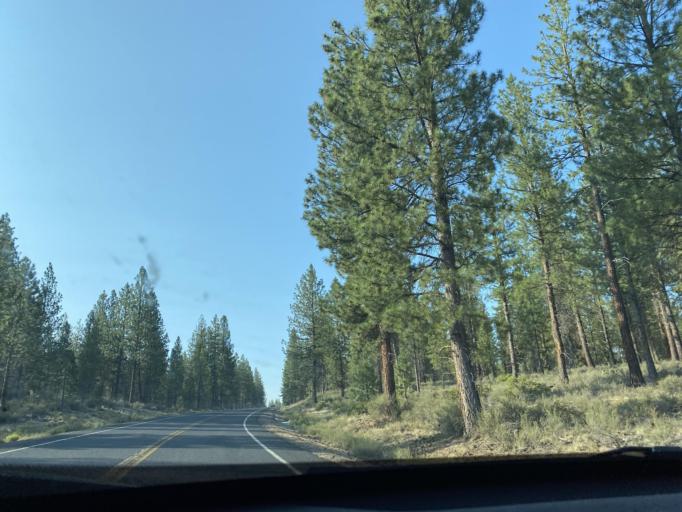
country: US
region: Oregon
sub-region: Deschutes County
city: La Pine
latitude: 43.7244
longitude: -121.4152
